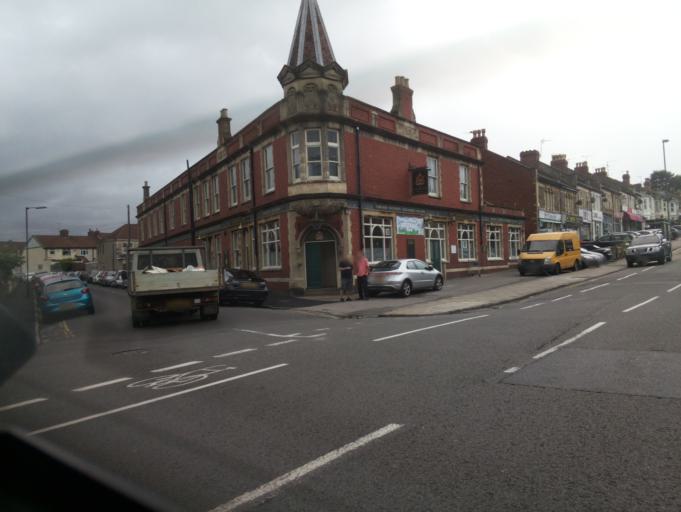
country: GB
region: England
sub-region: Bath and North East Somerset
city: Whitchurch
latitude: 51.4409
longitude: -2.5559
